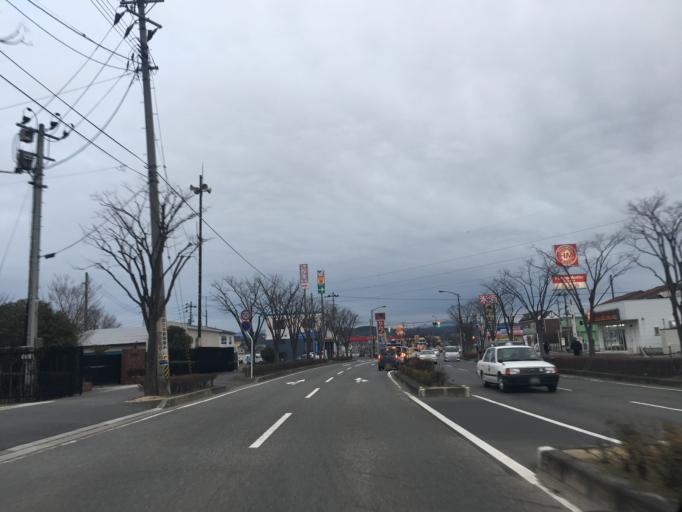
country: JP
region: Fukushima
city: Koriyama
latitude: 37.4000
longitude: 140.3990
